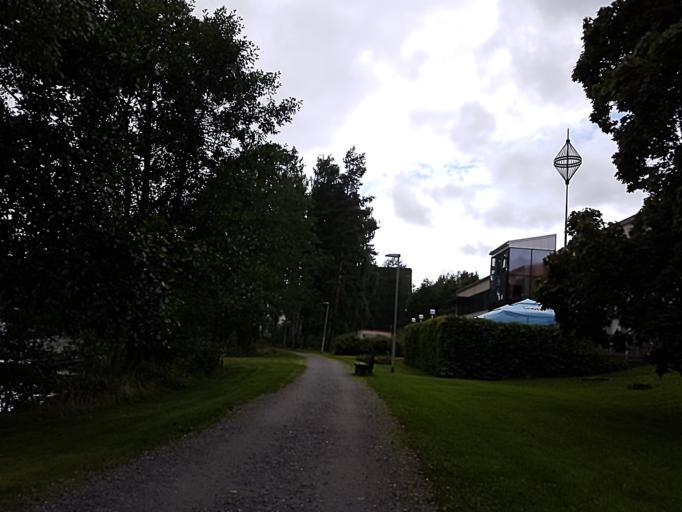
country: FI
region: Pirkanmaa
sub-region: Etelae-Pirkanmaa
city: Valkeakoski
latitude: 61.2710
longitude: 24.0398
